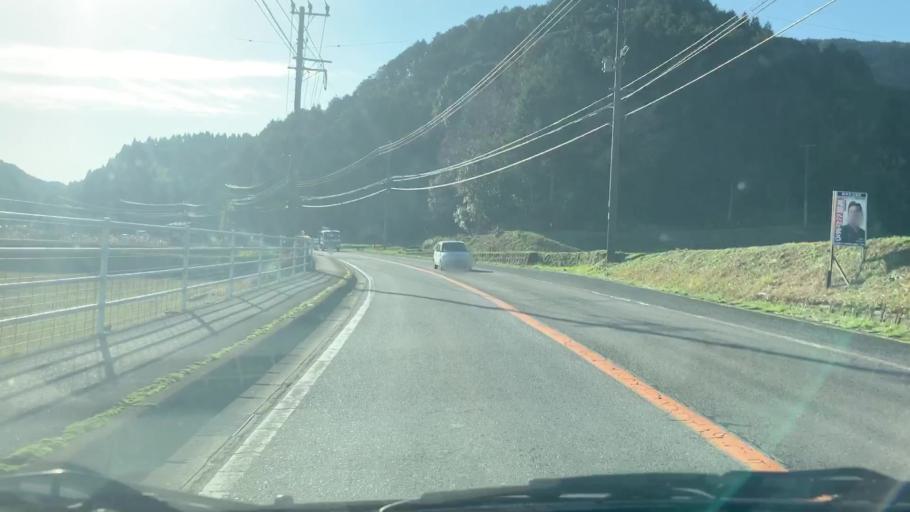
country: JP
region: Saga Prefecture
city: Takeocho-takeo
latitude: 33.2437
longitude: 130.0068
